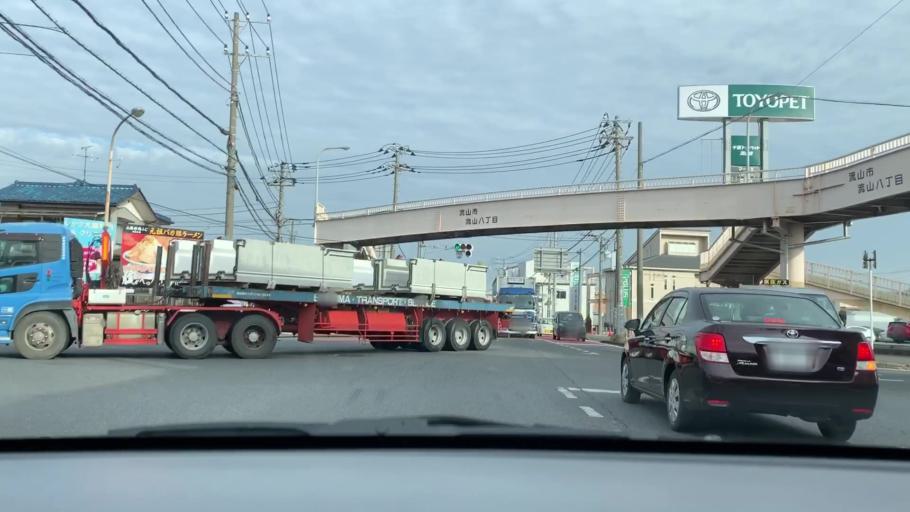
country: JP
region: Chiba
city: Nagareyama
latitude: 35.8443
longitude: 139.8977
